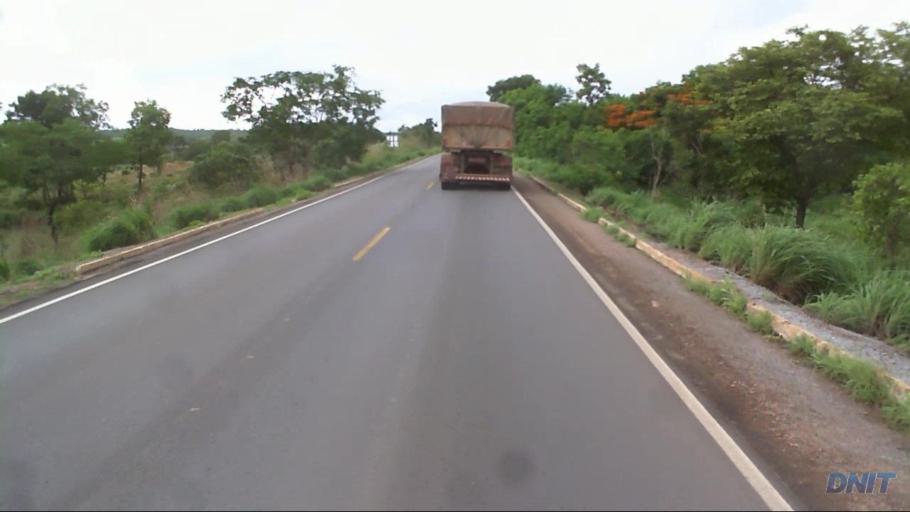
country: BR
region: Goias
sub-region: Padre Bernardo
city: Padre Bernardo
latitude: -15.1881
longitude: -48.2844
